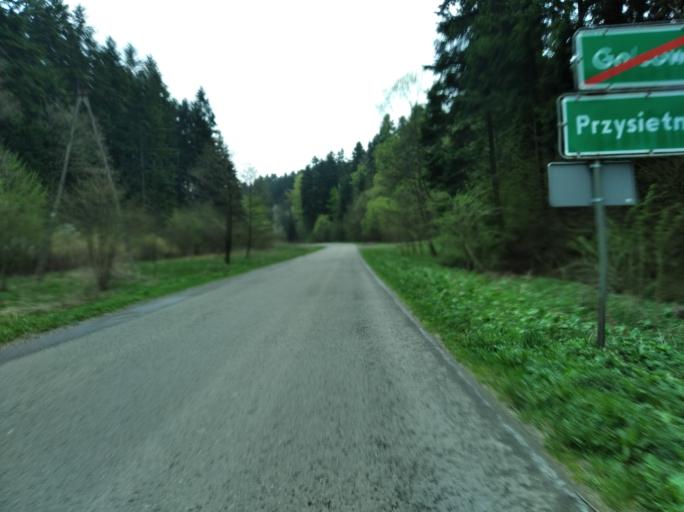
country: PL
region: Subcarpathian Voivodeship
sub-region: Powiat brzozowski
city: Golcowa
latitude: 49.7522
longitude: 22.0676
